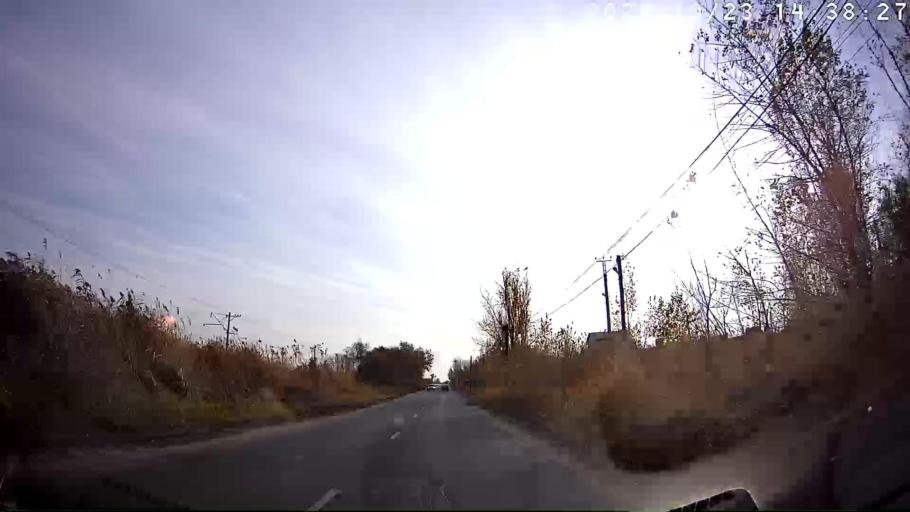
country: RU
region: Volgograd
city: Krasnoslobodsk
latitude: 48.4917
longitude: 44.5492
